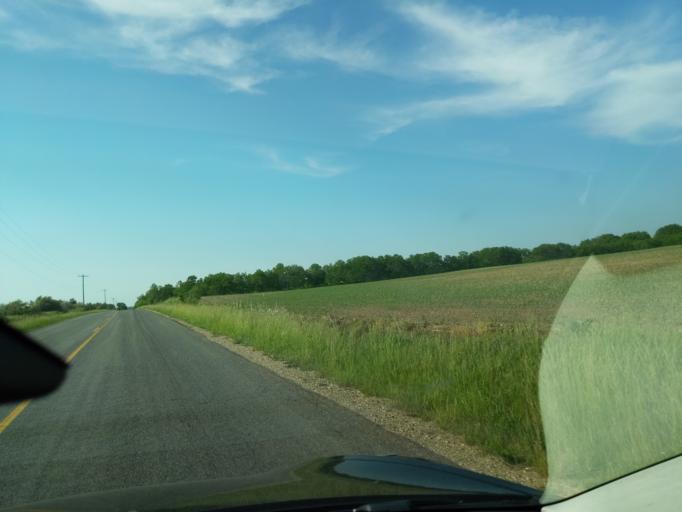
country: US
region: Michigan
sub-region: Barry County
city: Nashville
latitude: 42.6063
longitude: -85.1539
